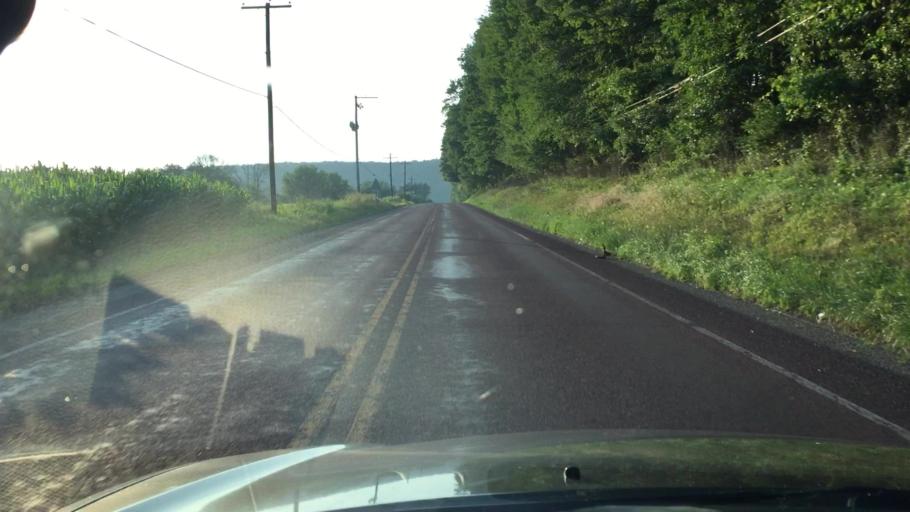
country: US
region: Pennsylvania
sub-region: Carbon County
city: Weatherly
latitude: 40.9205
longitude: -75.8602
